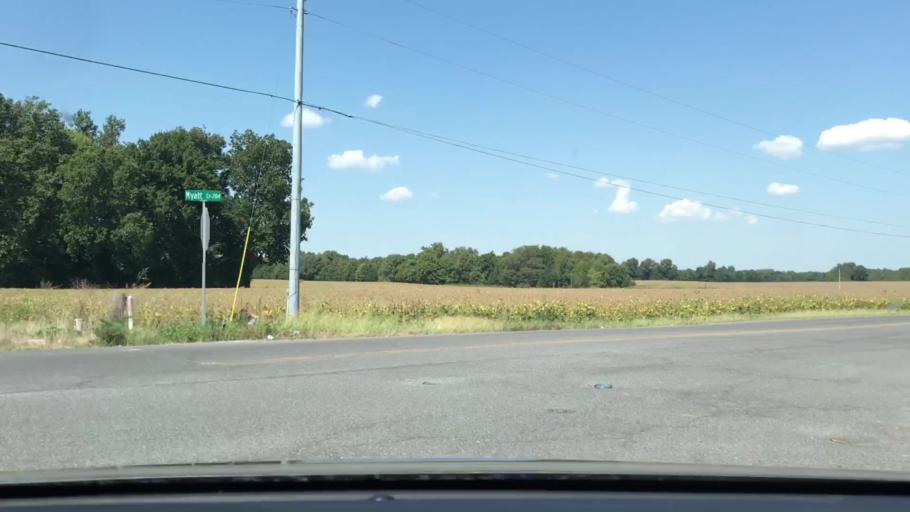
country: US
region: Kentucky
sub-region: Fulton County
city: Fulton
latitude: 36.5159
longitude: -88.9014
